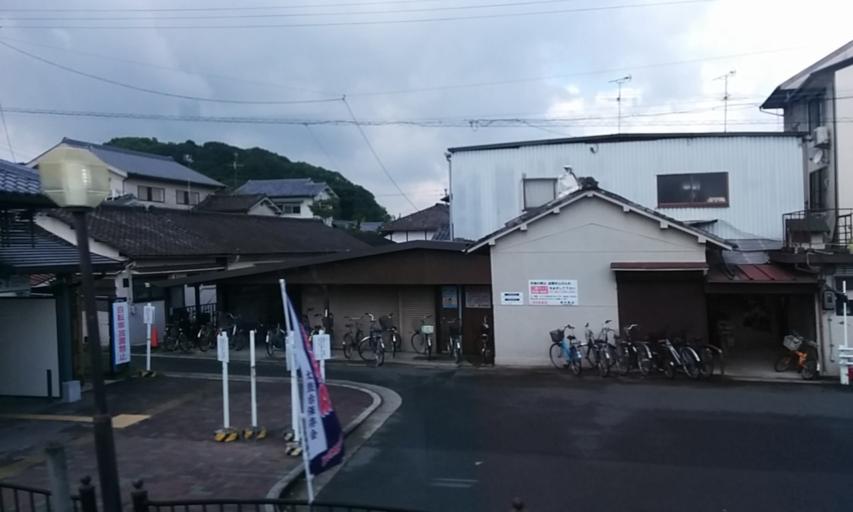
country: JP
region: Nara
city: Nara-shi
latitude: 34.6816
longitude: 135.7836
